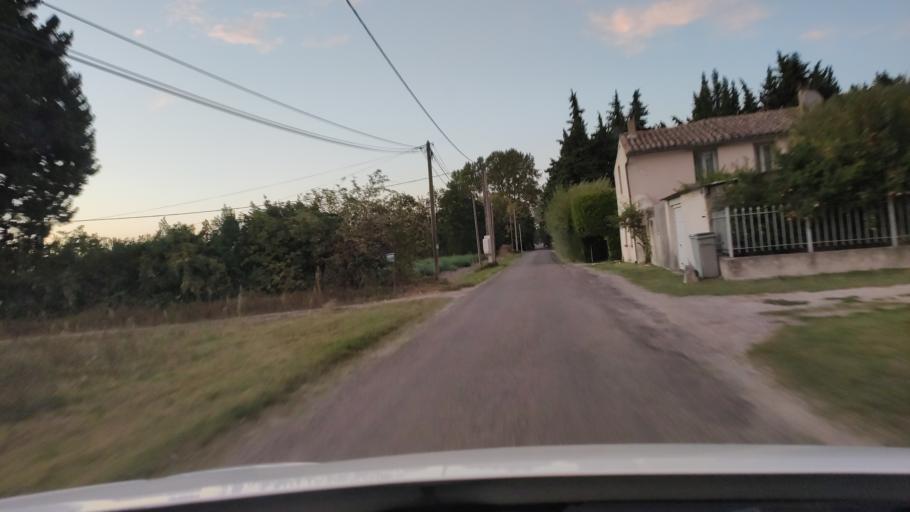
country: FR
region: Provence-Alpes-Cote d'Azur
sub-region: Departement du Vaucluse
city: Le Thor
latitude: 43.9512
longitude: 4.9715
